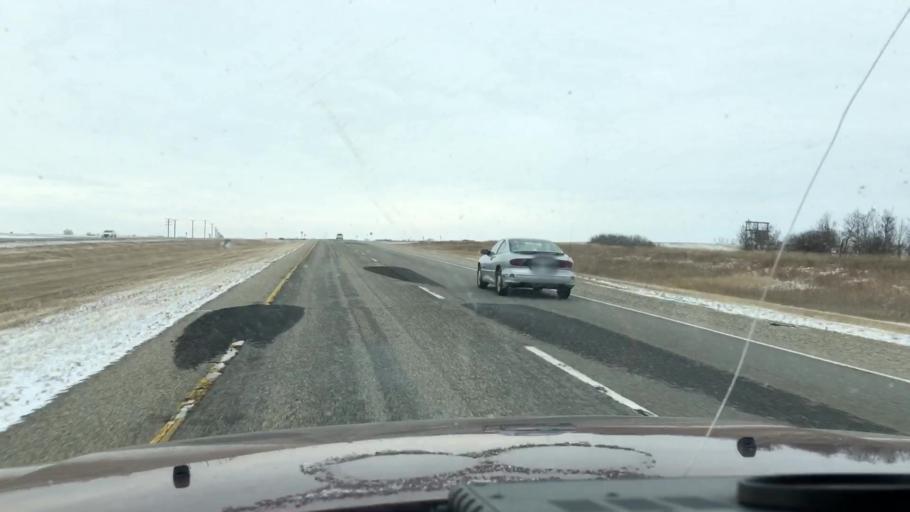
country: CA
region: Saskatchewan
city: Watrous
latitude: 51.4192
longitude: -106.1924
